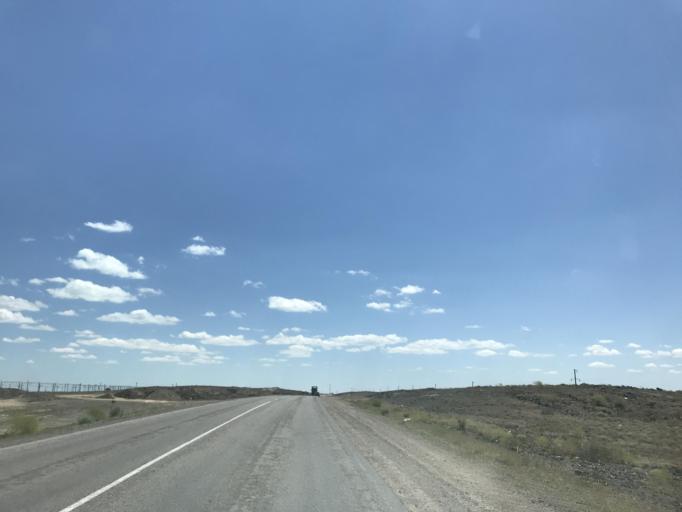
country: KZ
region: Almaty Oblysy
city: Ulken
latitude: 45.1874
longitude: 73.9177
